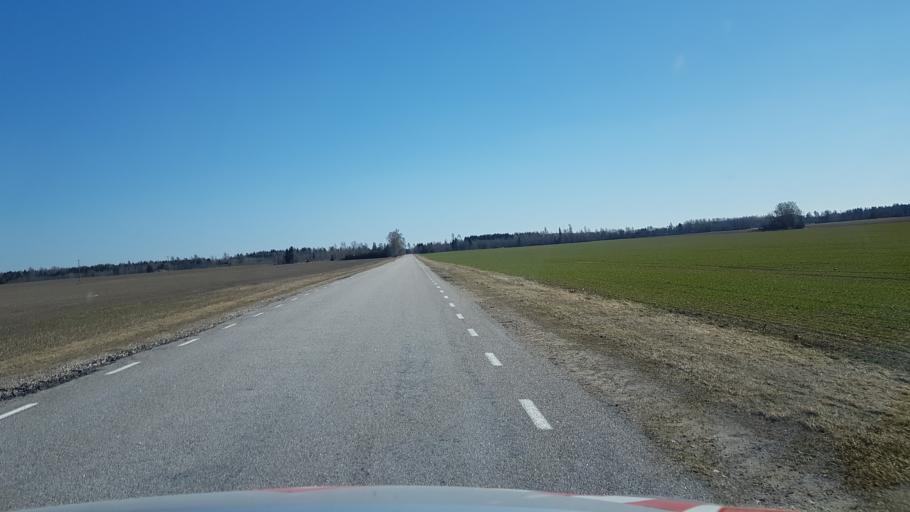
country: EE
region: Laeaene-Virumaa
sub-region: Vaeike-Maarja vald
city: Vaike-Maarja
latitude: 59.1046
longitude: 26.3878
